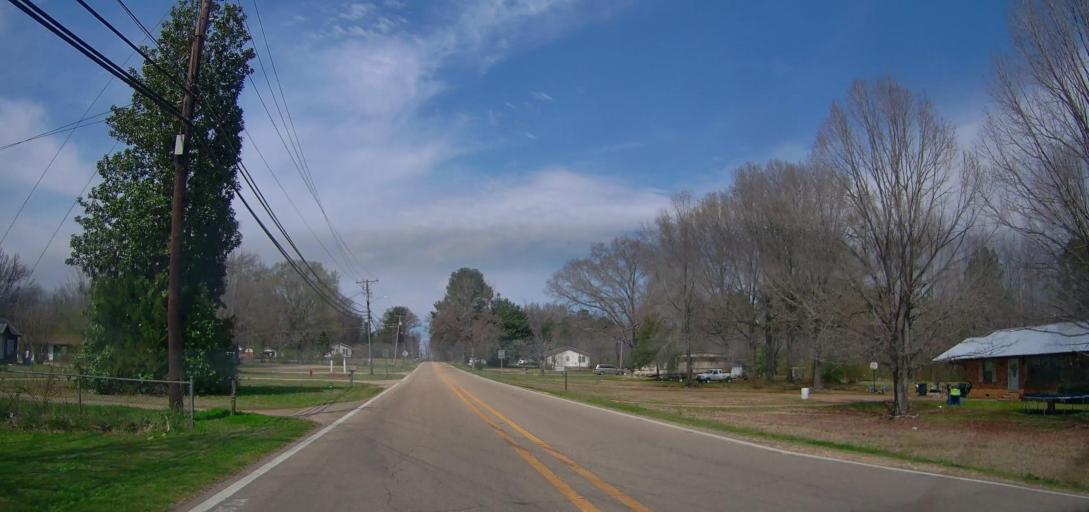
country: US
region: Mississippi
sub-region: Union County
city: New Albany
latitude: 34.4742
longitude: -88.9943
